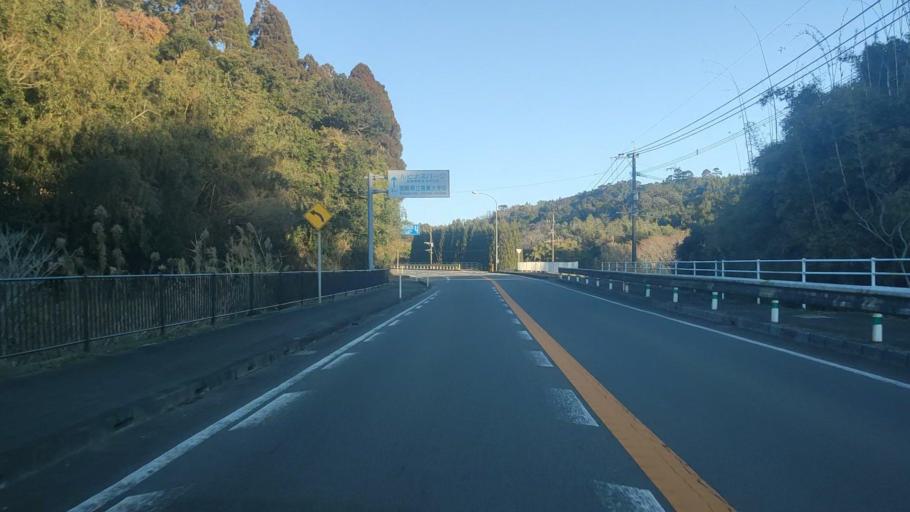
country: JP
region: Miyazaki
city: Takanabe
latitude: 32.1494
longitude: 131.5250
